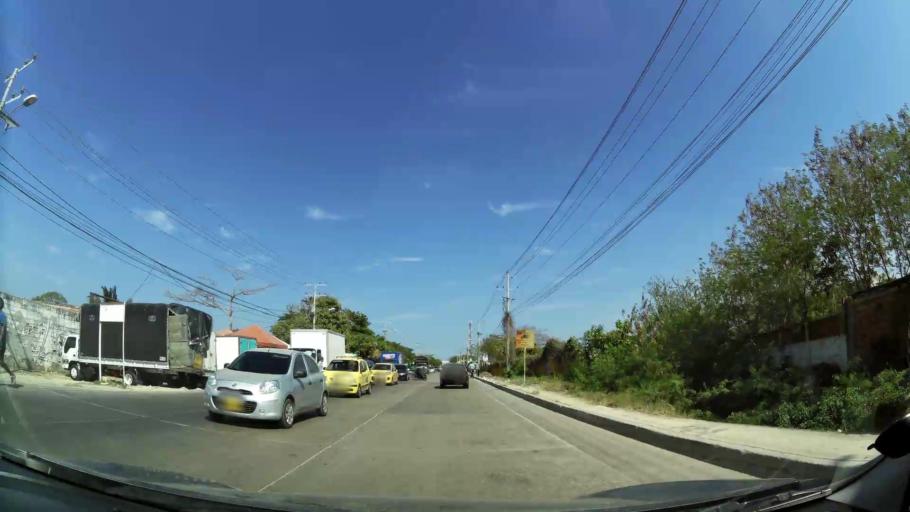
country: CO
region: Atlantico
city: Barranquilla
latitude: 10.9436
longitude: -74.8297
